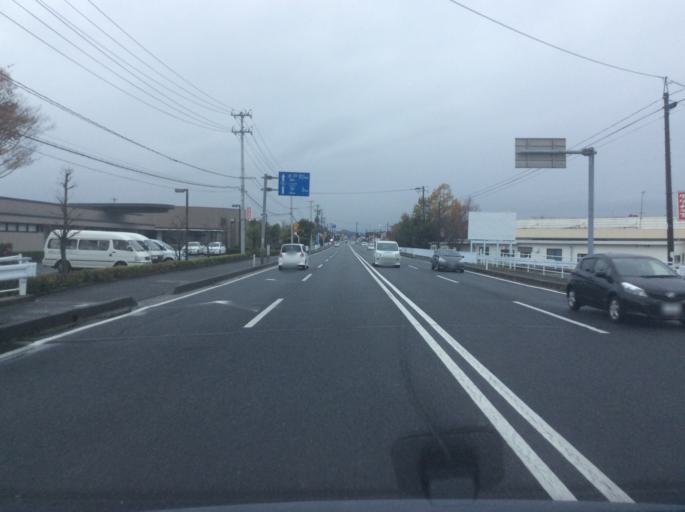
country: JP
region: Fukushima
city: Iwaki
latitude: 37.0909
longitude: 140.9727
